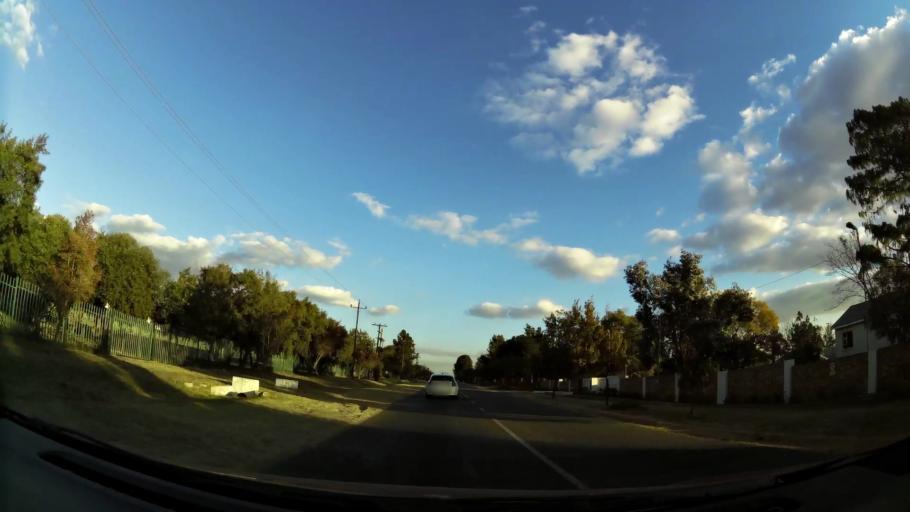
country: ZA
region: Gauteng
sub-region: City of Johannesburg Metropolitan Municipality
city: Midrand
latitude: -25.9697
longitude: 28.1535
